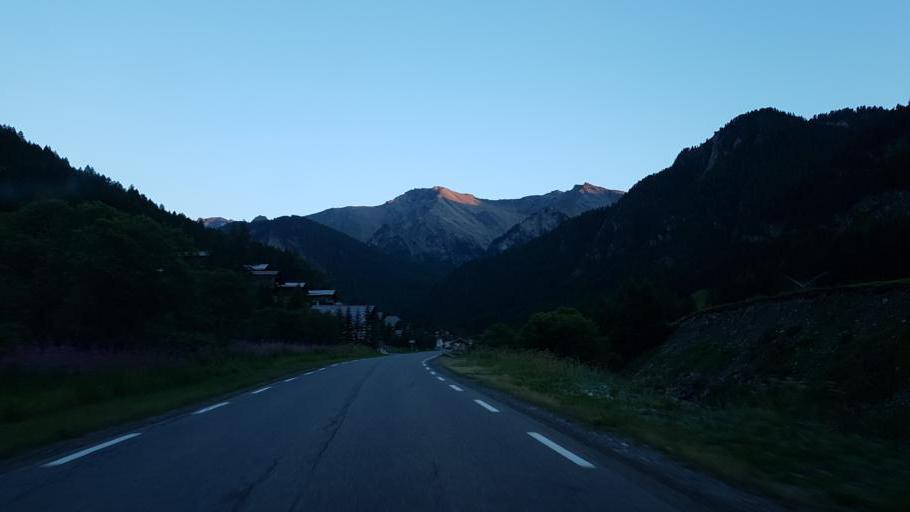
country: IT
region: Piedmont
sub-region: Provincia di Cuneo
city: Pontechianale
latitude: 44.7150
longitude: 6.8481
